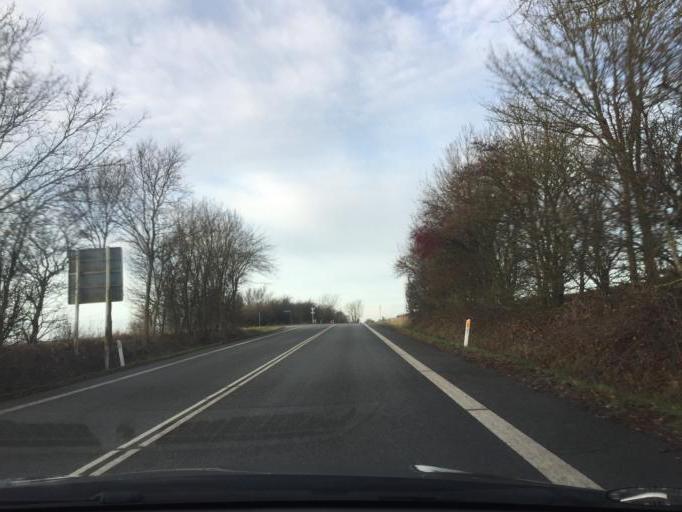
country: DK
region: South Denmark
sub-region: Faaborg-Midtfyn Kommune
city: Ringe
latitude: 55.2576
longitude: 10.4663
